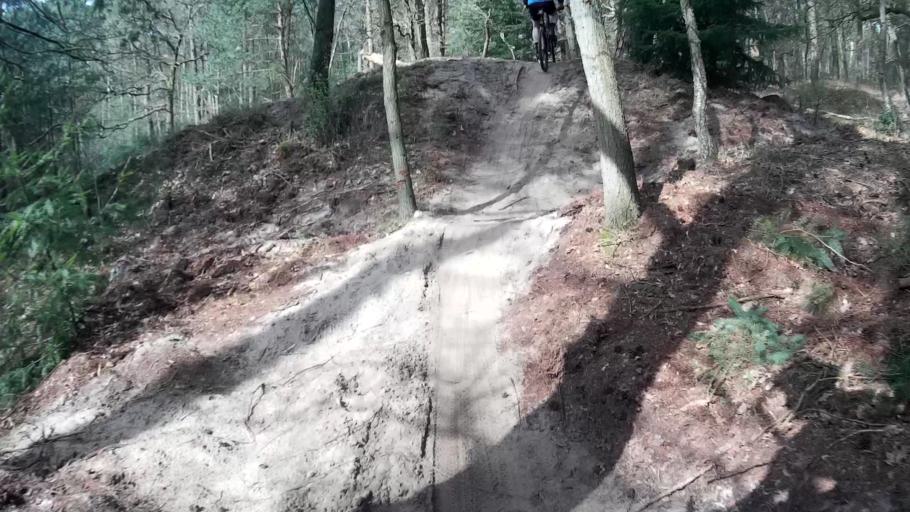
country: NL
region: Utrecht
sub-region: Gemeente Utrechtse Heuvelrug
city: Driebergen-Rijsenburg
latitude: 52.0688
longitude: 5.2935
